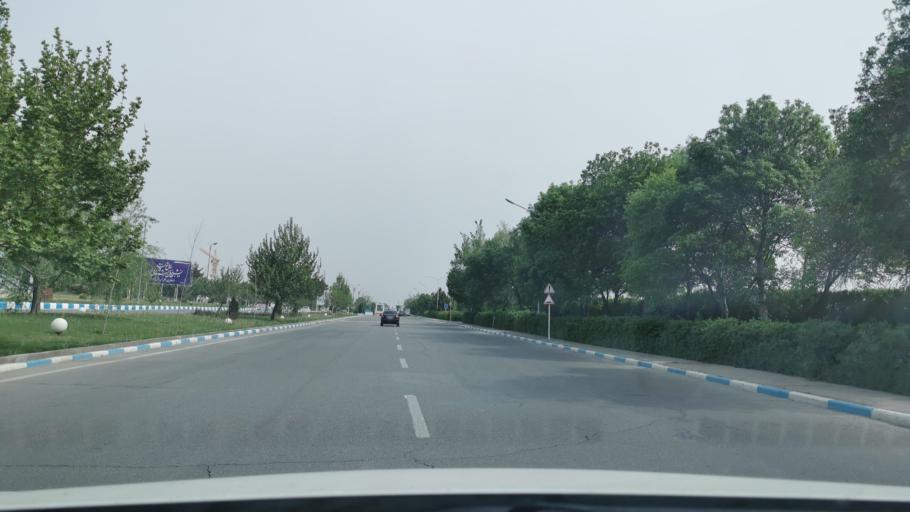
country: IR
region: Razavi Khorasan
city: Mashhad
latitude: 36.2310
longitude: 59.6358
